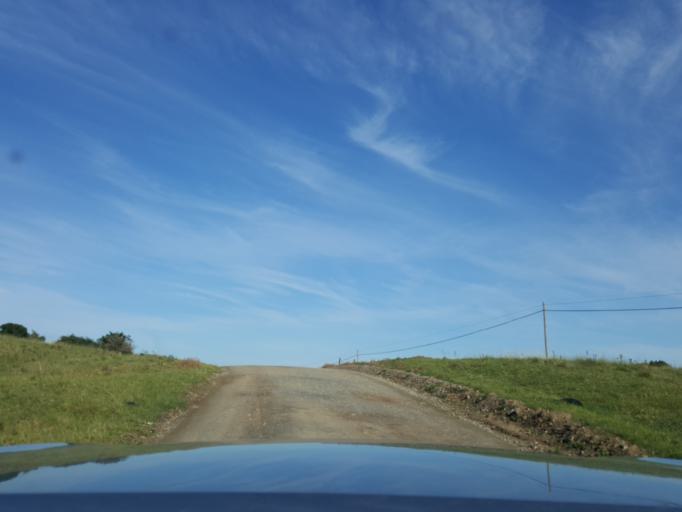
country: ZA
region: Eastern Cape
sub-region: Cacadu District Municipality
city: Port Alfred
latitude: -33.6431
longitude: 26.7341
